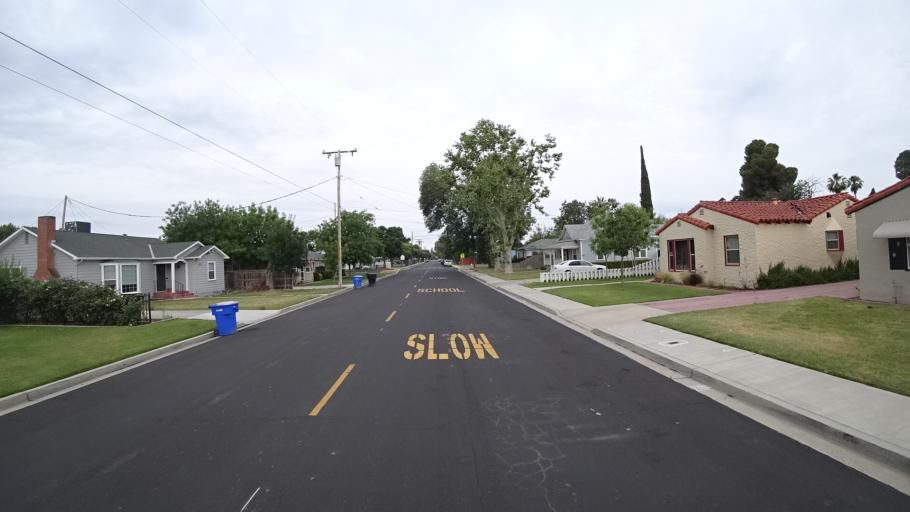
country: US
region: California
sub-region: Kings County
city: Hanford
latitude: 36.3390
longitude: -119.6512
